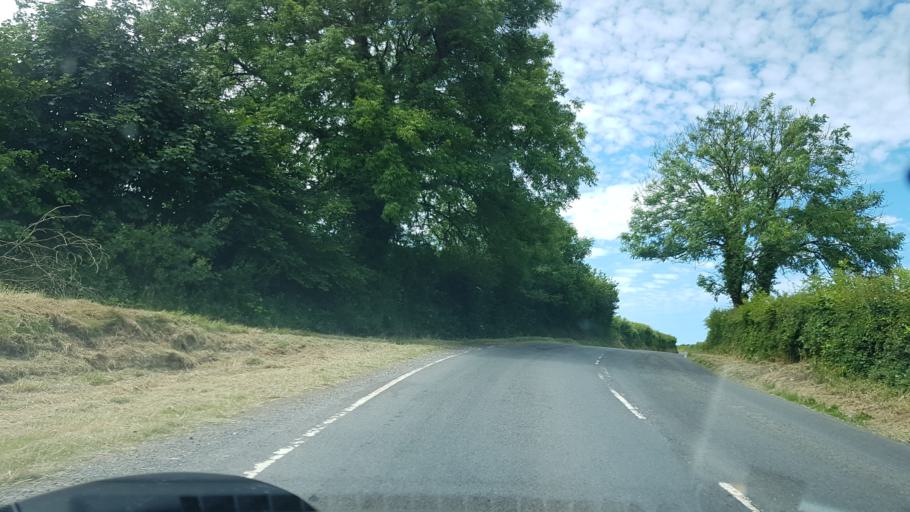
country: GB
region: Wales
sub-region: Carmarthenshire
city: Whitland
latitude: 51.7817
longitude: -4.6288
